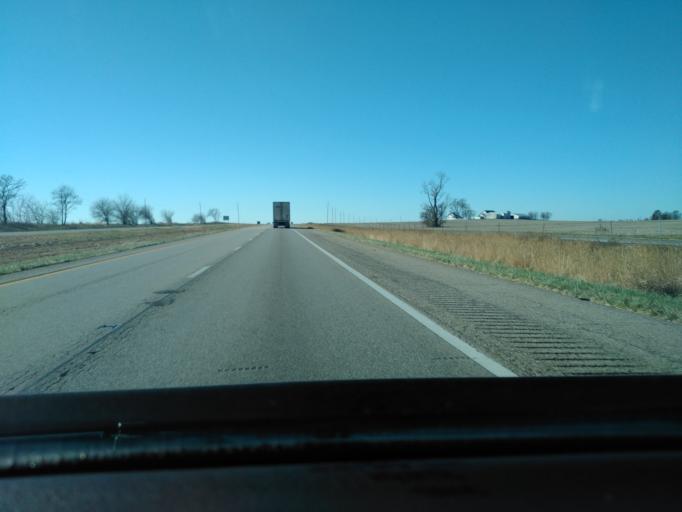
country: US
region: Illinois
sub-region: Madison County
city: Highland
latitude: 38.8218
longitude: -89.5587
